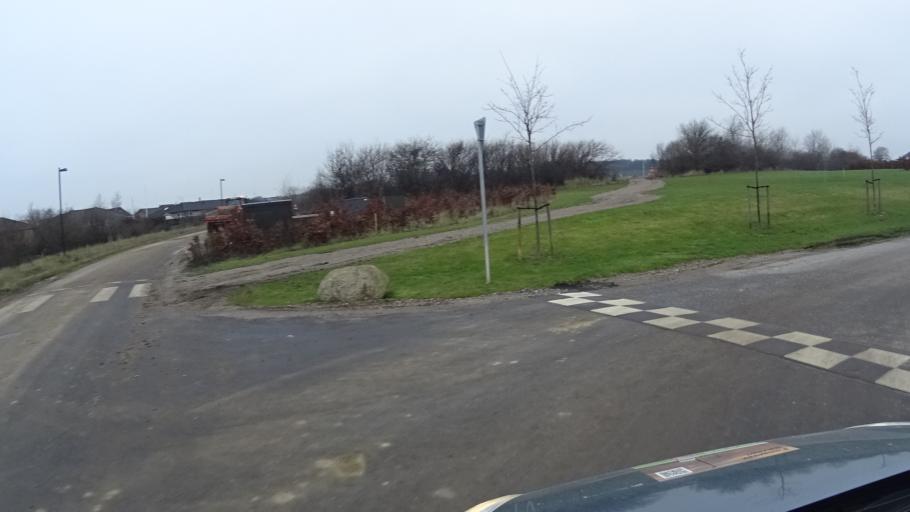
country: DK
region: South Denmark
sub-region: Vejle Kommune
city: Vejle
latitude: 55.7293
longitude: 9.6168
